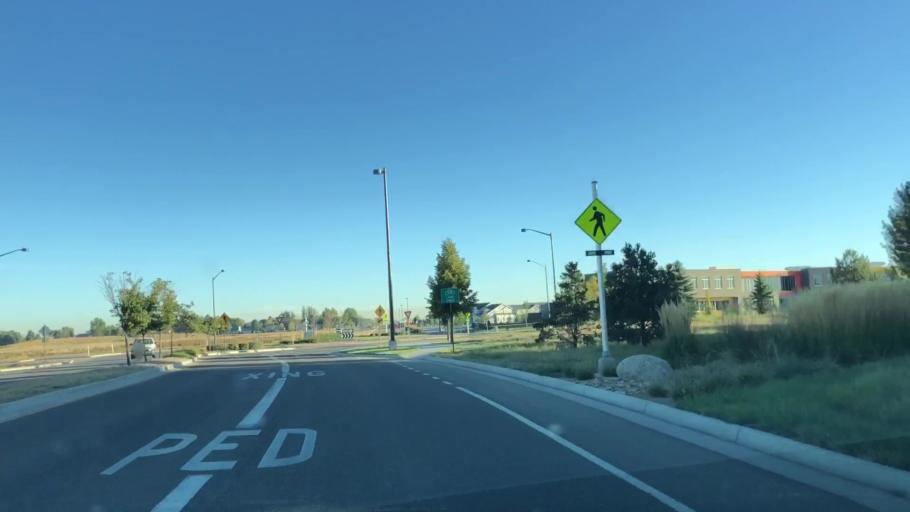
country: US
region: Colorado
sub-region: Larimer County
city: Loveland
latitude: 40.4135
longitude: -105.0209
